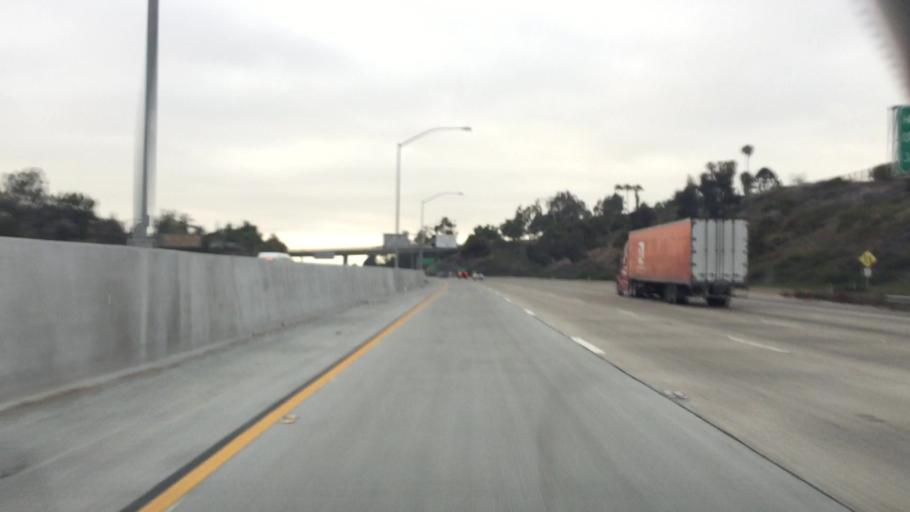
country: US
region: California
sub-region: San Diego County
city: Bonita
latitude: 32.6305
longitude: -117.0444
